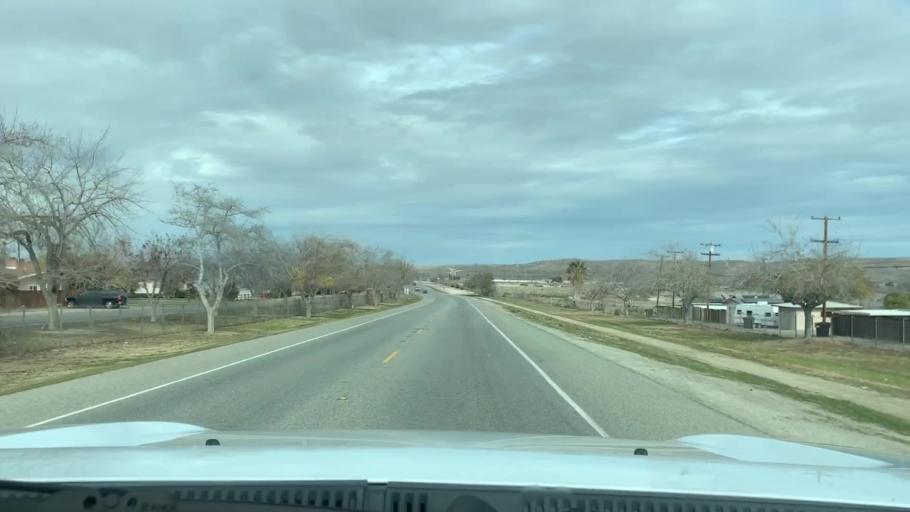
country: US
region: California
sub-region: Kern County
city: Taft
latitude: 35.1430
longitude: -119.4472
